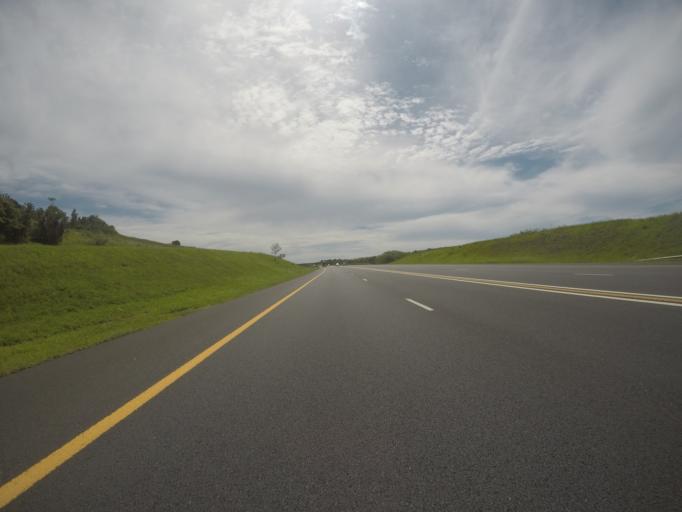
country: ZA
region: KwaZulu-Natal
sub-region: iLembe District Municipality
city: Mandeni
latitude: -29.1659
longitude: 31.5278
